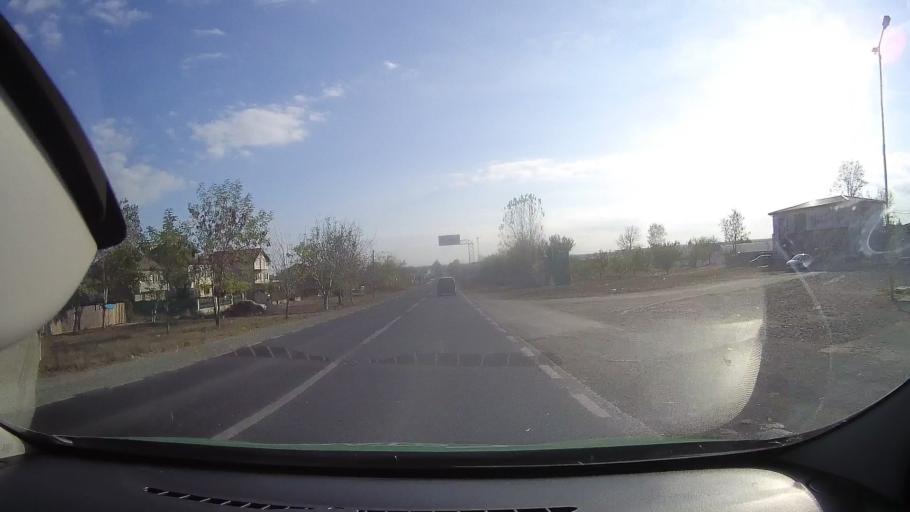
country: RO
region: Constanta
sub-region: Comuna Lumina
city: Lumina
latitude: 44.2870
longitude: 28.5566
